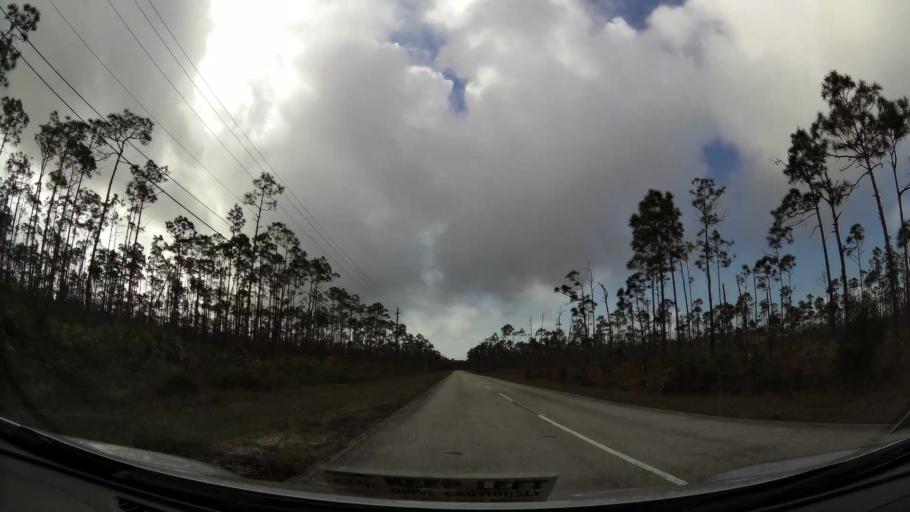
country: BS
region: Freeport
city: Lucaya
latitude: 26.5938
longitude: -78.5470
